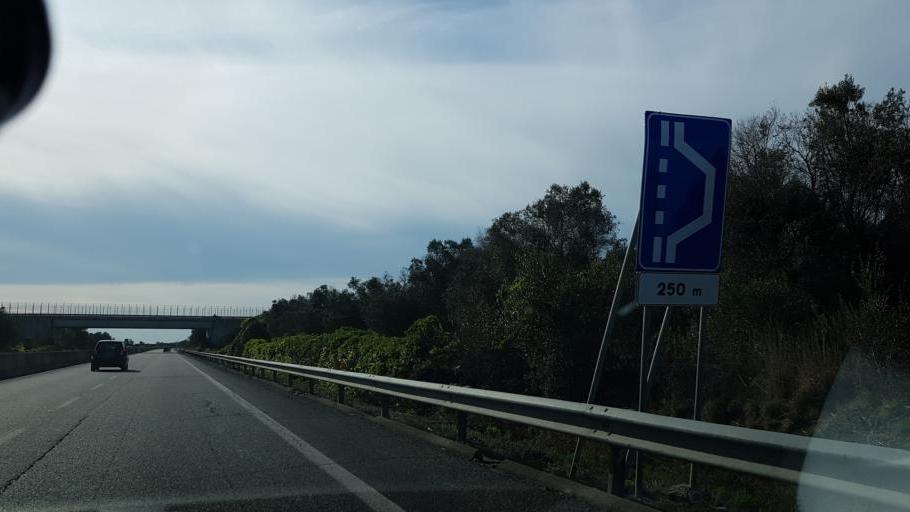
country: IT
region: Apulia
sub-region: Provincia di Brindisi
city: San Pietro Vernotico
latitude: 40.5368
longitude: 18.0059
